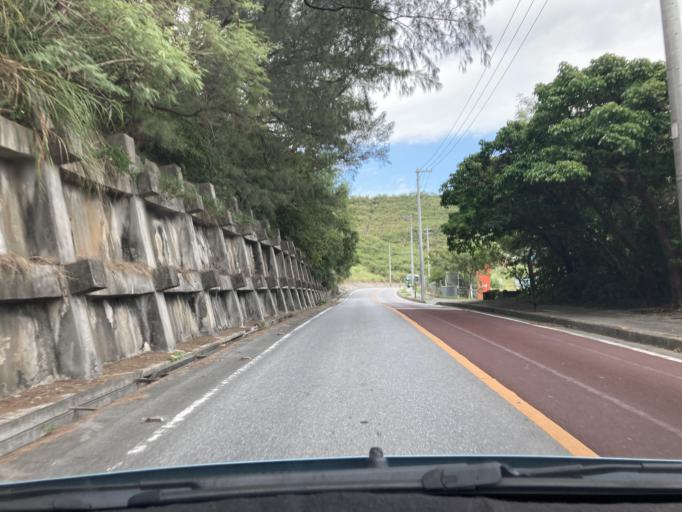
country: JP
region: Okinawa
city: Ginowan
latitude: 26.2618
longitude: 127.7837
